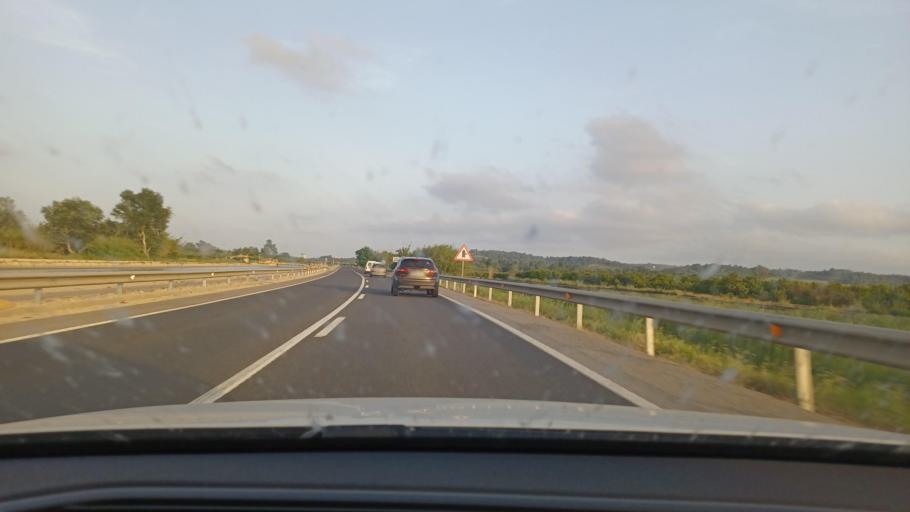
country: ES
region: Catalonia
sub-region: Provincia de Tarragona
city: Masdenverge
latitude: 40.7557
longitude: 0.5393
